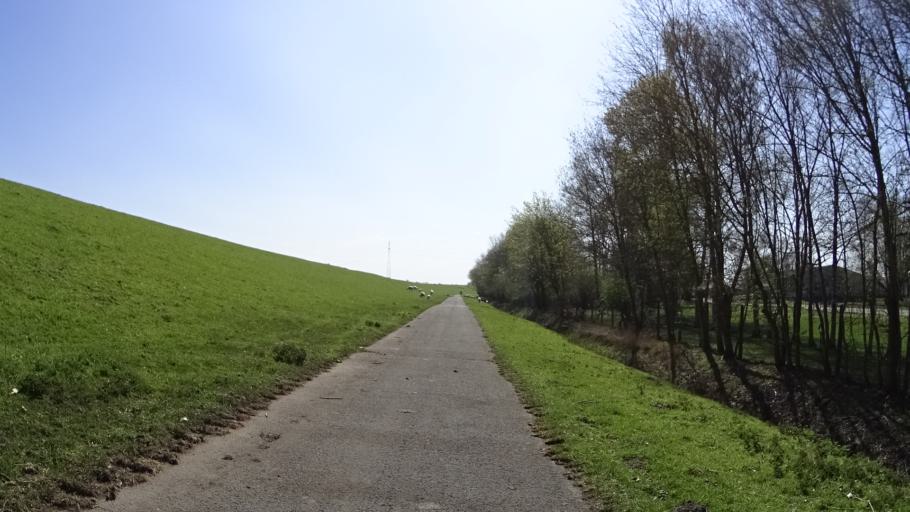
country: DE
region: Lower Saxony
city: Weener
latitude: 53.1591
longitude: 7.3715
